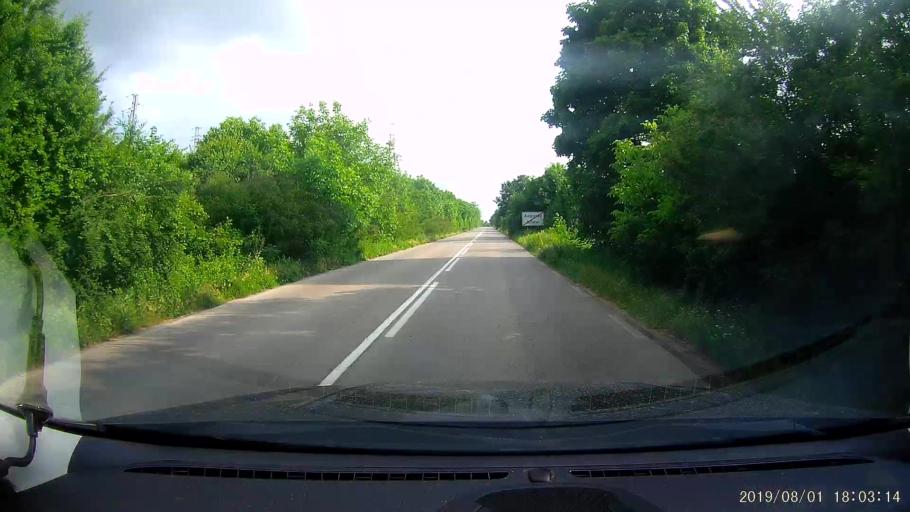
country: BG
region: Silistra
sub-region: Obshtina Alfatar
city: Alfatar
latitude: 43.9321
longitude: 27.2901
